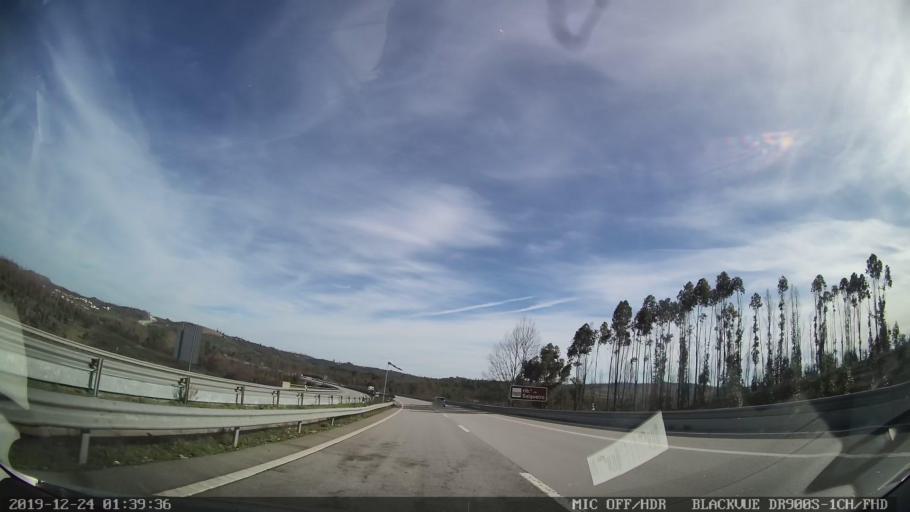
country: PT
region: Portalegre
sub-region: Gaviao
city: Gaviao
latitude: 39.5337
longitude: -7.9039
